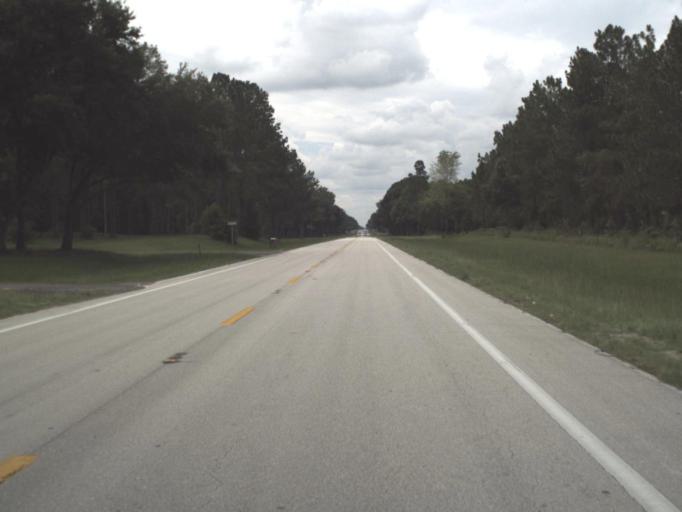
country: US
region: Florida
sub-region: Alachua County
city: High Springs
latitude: 29.7391
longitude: -82.6072
